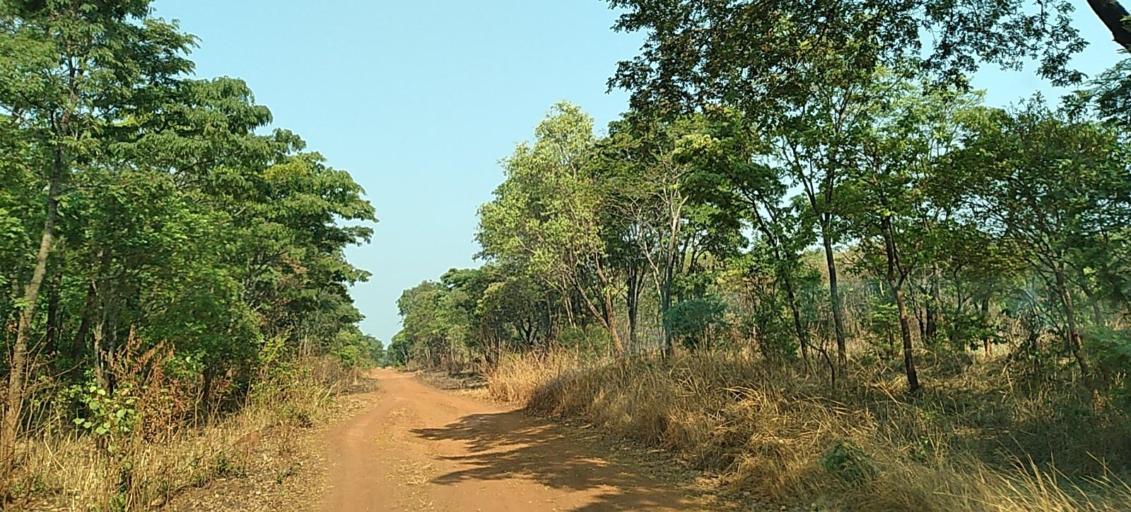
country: ZM
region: Copperbelt
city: Chingola
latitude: -12.8863
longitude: 27.4205
